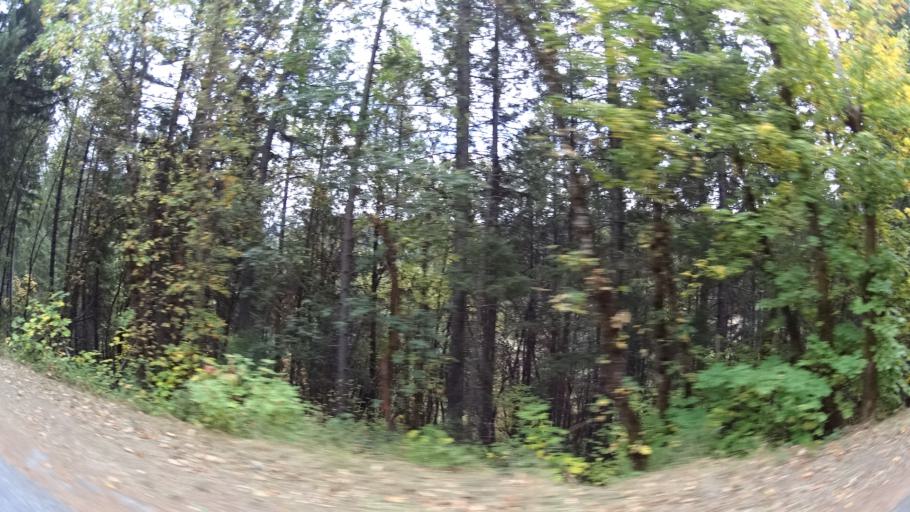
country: US
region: California
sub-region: Siskiyou County
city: Happy Camp
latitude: 41.7798
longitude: -123.3462
